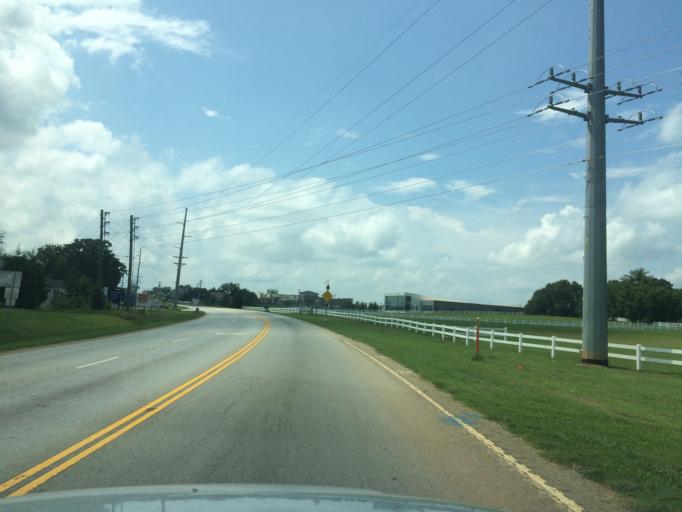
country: US
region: South Carolina
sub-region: Greenville County
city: Five Forks
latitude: 34.8074
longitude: -82.2187
